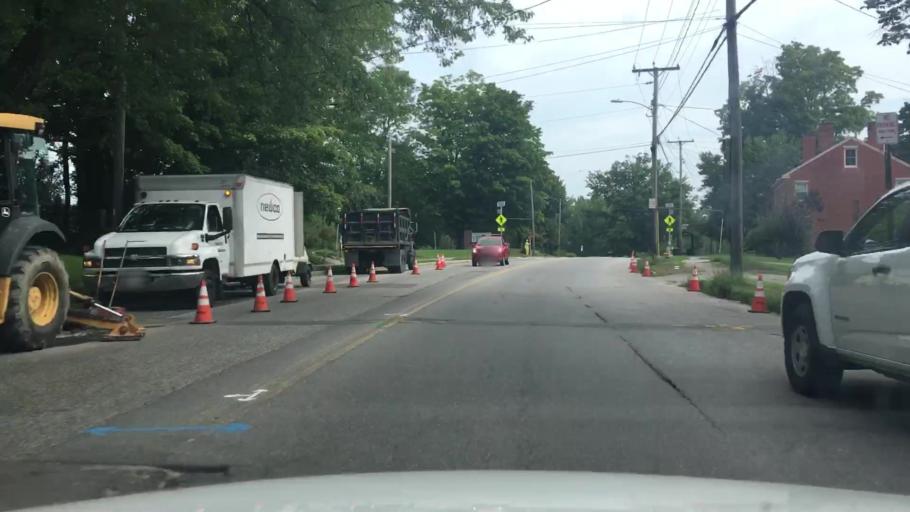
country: US
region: Maine
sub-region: Cumberland County
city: Portland
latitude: 43.6943
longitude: -70.2922
